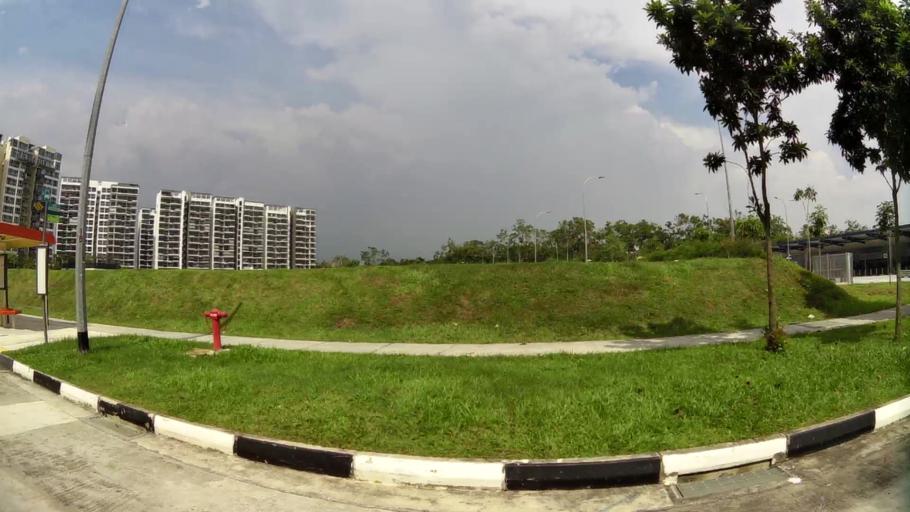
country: SG
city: Singapore
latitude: 1.3574
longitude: 103.9409
